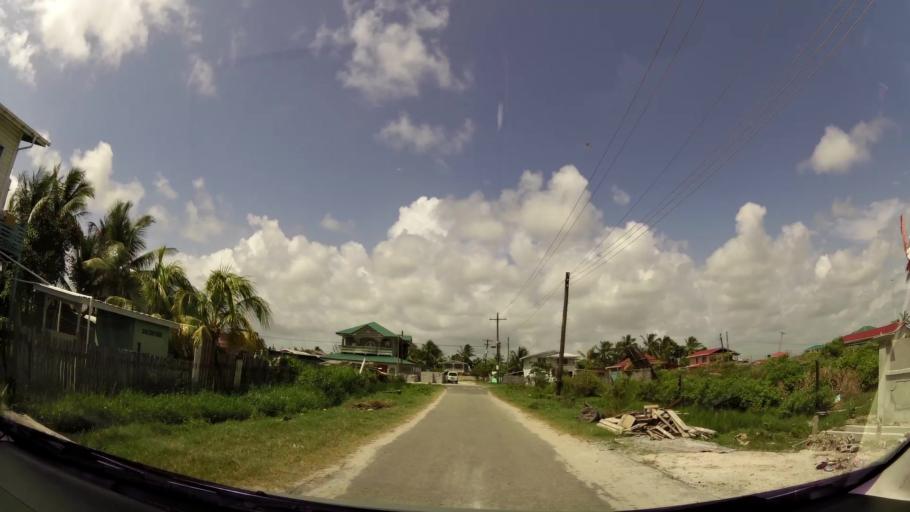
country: GY
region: Demerara-Mahaica
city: Mahaica Village
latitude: 6.7725
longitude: -58.0137
